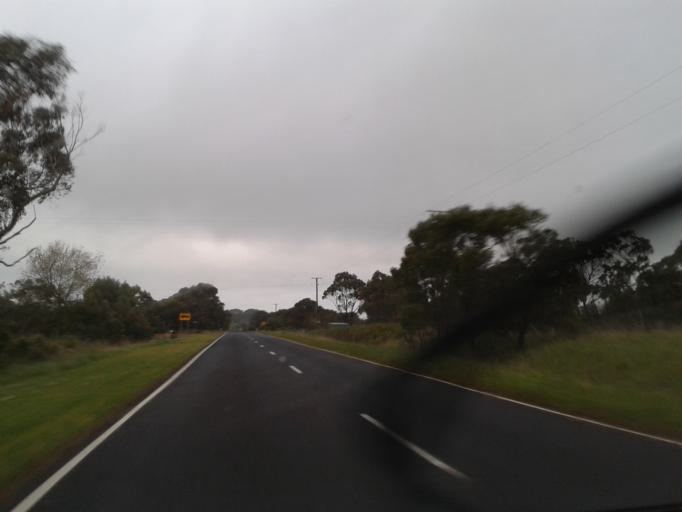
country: AU
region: Victoria
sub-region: Glenelg
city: Portland
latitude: -38.3439
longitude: 141.5508
